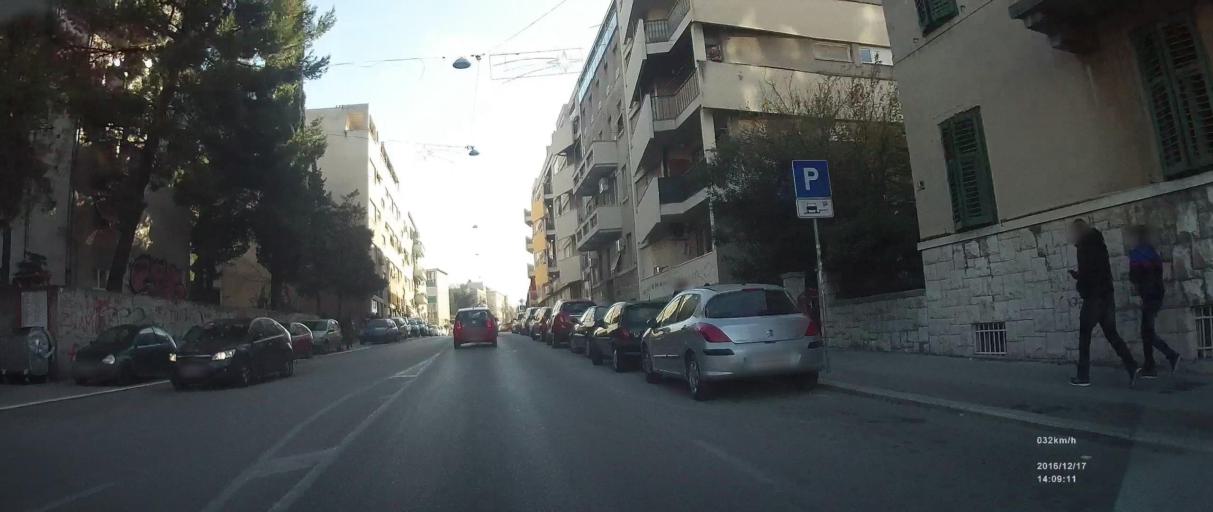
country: HR
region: Splitsko-Dalmatinska
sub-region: Grad Split
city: Split
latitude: 43.5175
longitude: 16.4347
